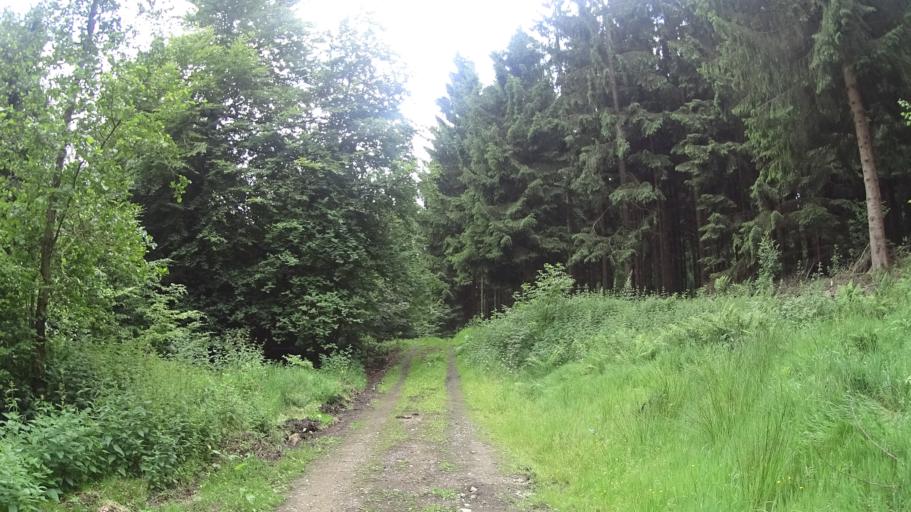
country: DE
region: Lower Saxony
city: Hameln
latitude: 52.1642
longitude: 9.3968
